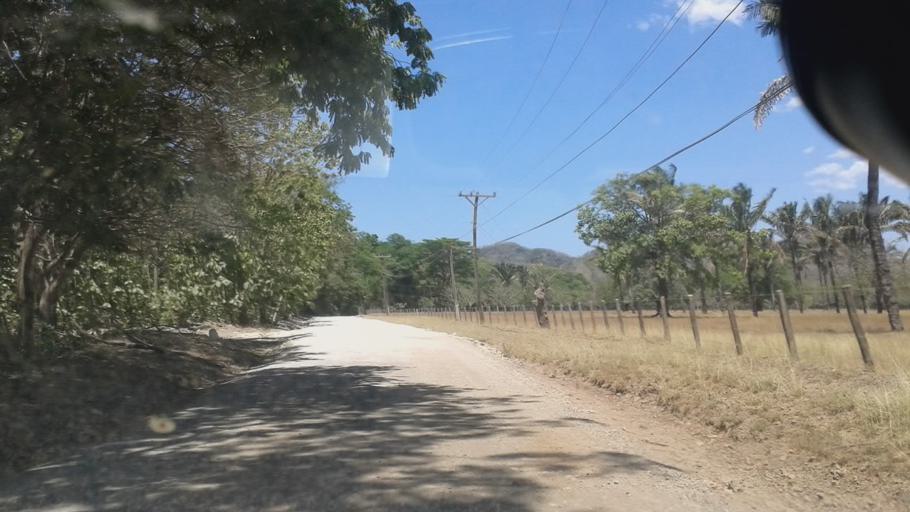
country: CR
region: Guanacaste
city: Samara
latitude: 9.9984
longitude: -85.6910
